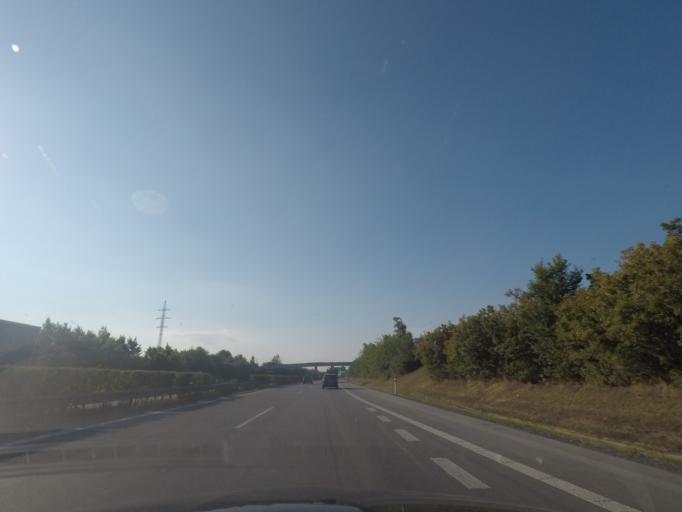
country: CZ
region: Olomoucky
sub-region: Okres Olomouc
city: Olomouc
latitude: 49.5579
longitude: 17.2241
